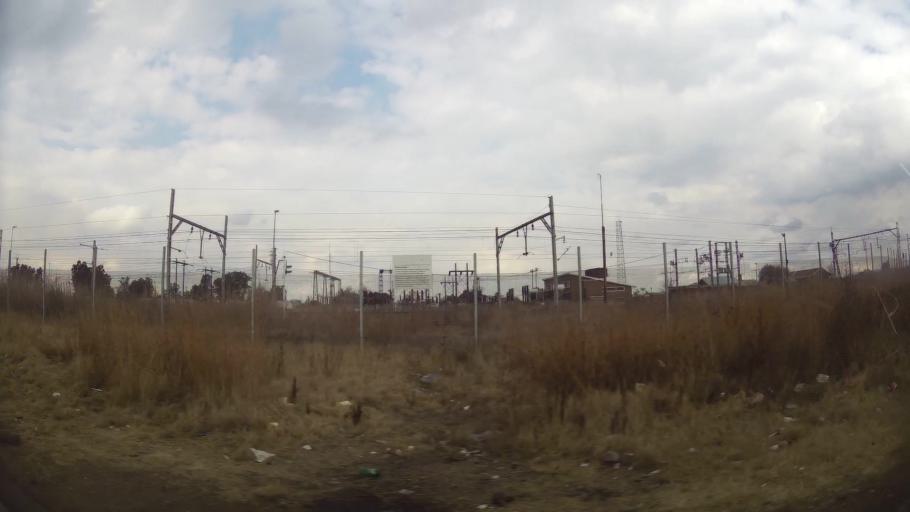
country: ZA
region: Orange Free State
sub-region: Fezile Dabi District Municipality
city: Sasolburg
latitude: -26.8451
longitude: 27.8714
